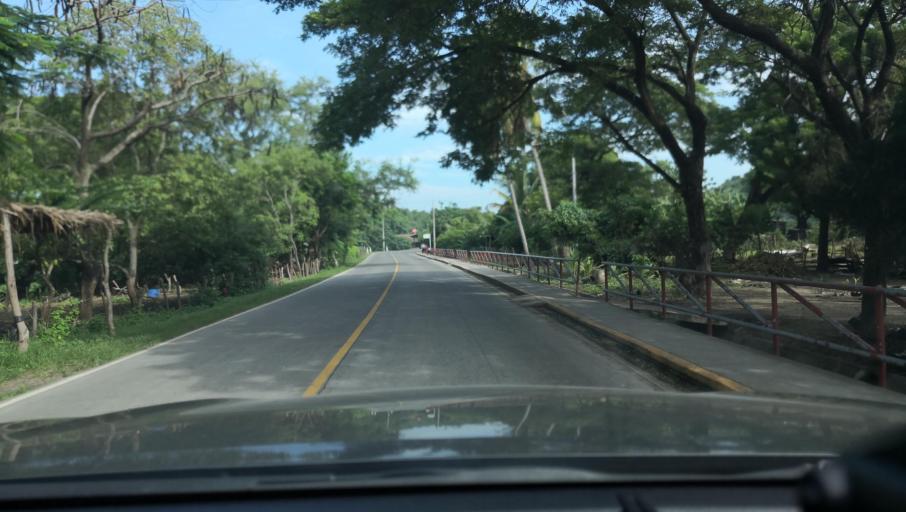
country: NI
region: Masaya
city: Tisma
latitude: 12.1493
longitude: -85.8393
